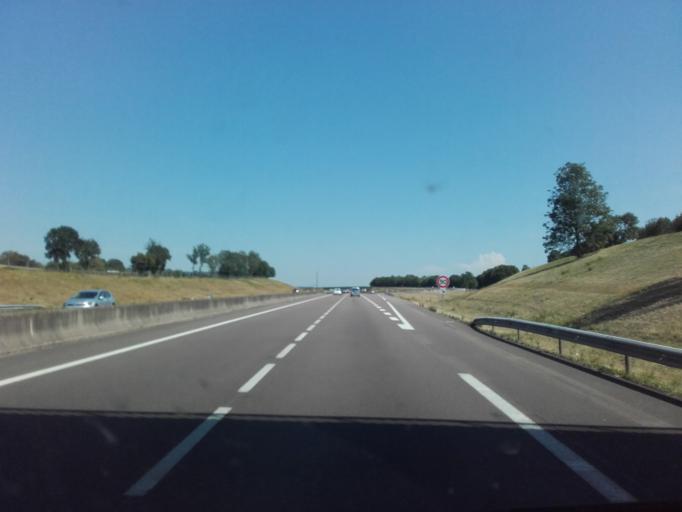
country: FR
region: Bourgogne
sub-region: Departement de la Cote-d'Or
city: Pouilly-en-Auxois
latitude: 47.2535
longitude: 4.5484
